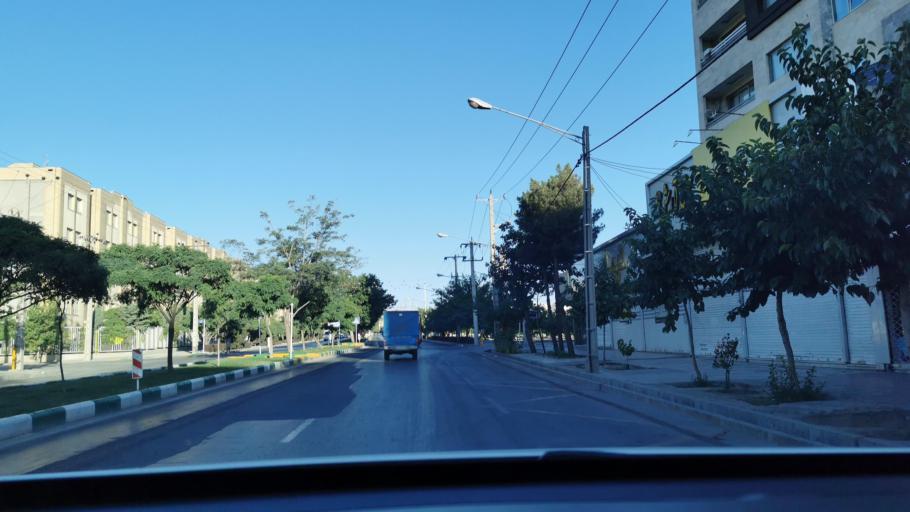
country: IR
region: Razavi Khorasan
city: Mashhad
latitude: 36.3523
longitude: 59.4948
